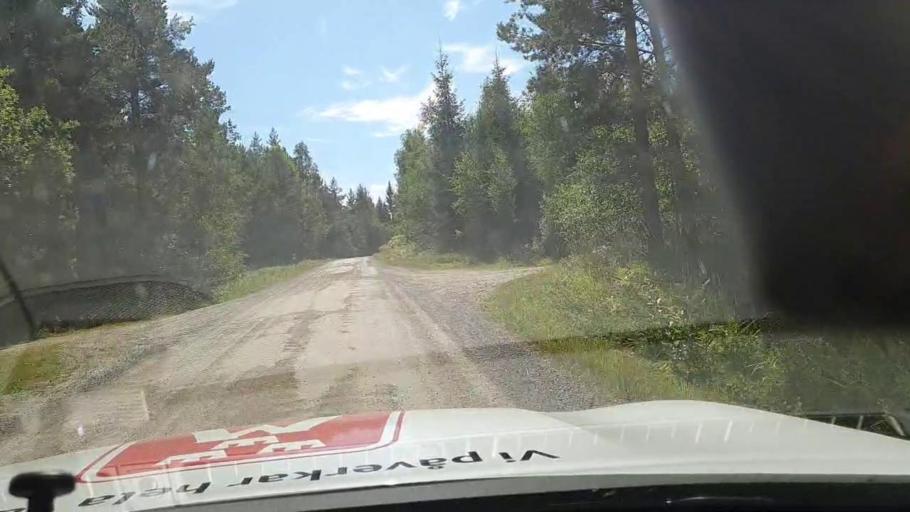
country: SE
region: Soedermanland
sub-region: Strangnas Kommun
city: Akers Styckebruk
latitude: 59.2176
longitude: 16.9090
